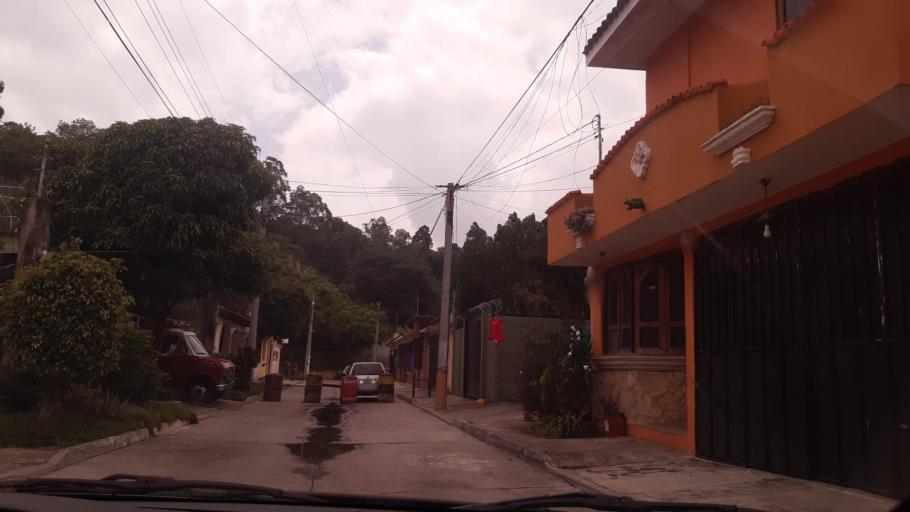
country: GT
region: Guatemala
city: Petapa
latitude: 14.5084
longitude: -90.5453
